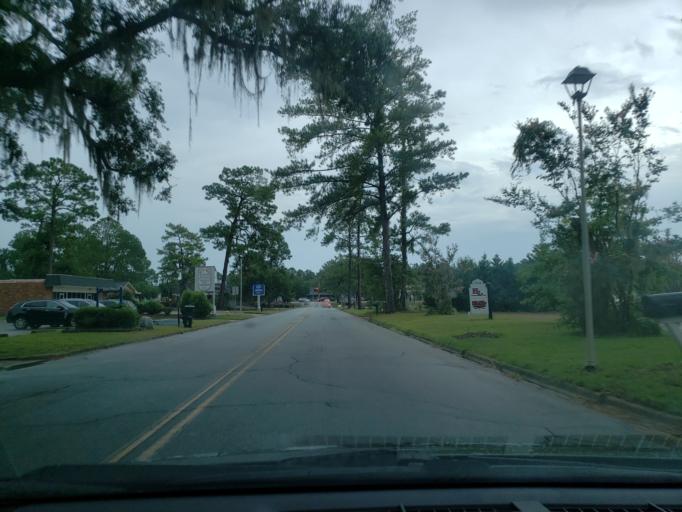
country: US
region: Georgia
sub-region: Dougherty County
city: Albany
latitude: 31.6049
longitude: -84.1781
